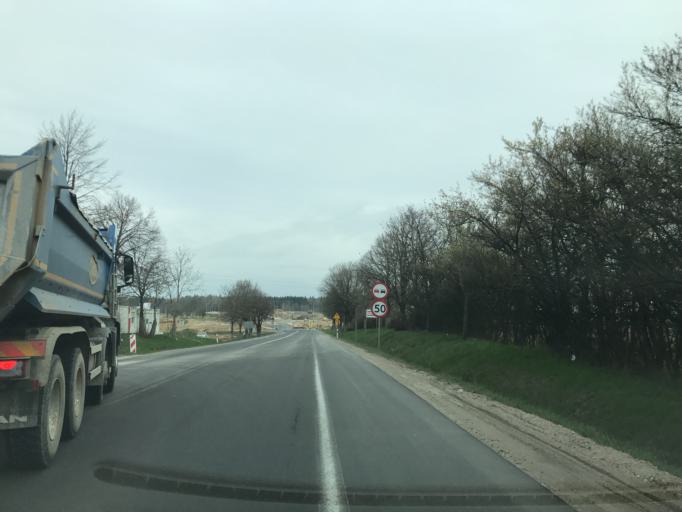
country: PL
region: Warmian-Masurian Voivodeship
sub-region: Powiat ostrodzki
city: Gierzwald
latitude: 53.5952
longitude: 20.0818
